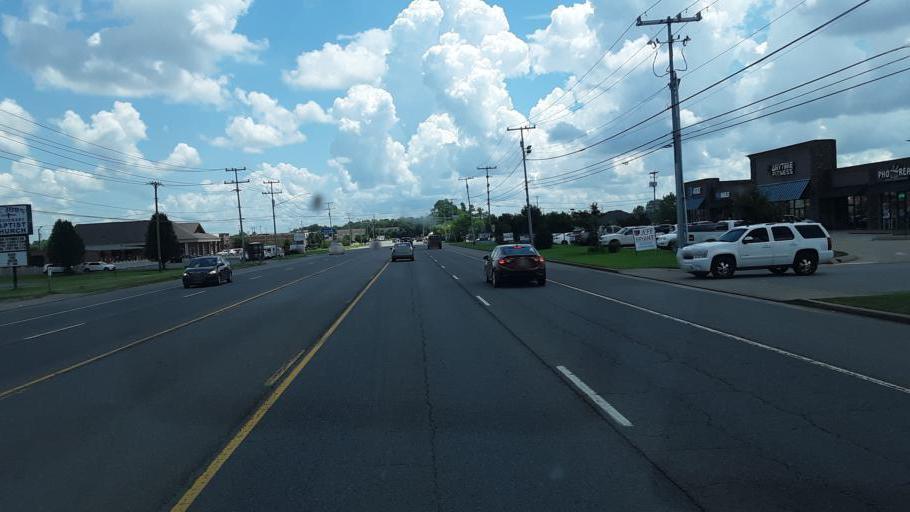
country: US
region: Tennessee
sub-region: Montgomery County
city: Clarksville
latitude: 36.6255
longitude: -87.3230
